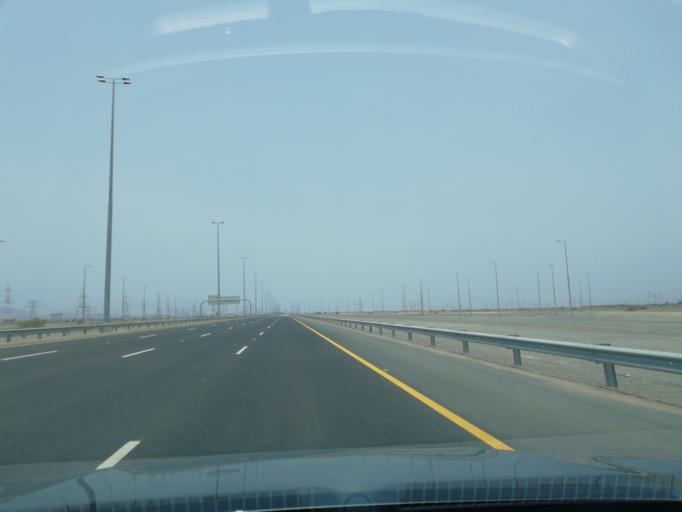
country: OM
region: Al Batinah
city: Al Liwa'
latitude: 24.4032
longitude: 56.5420
